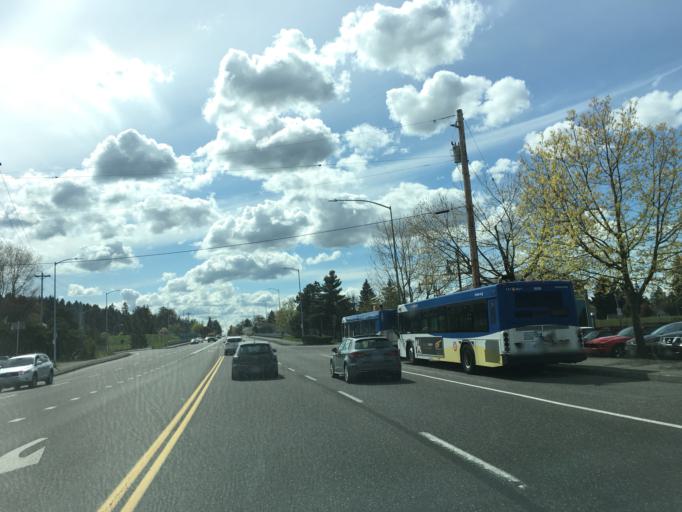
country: US
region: Oregon
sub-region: Multnomah County
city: Lents
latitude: 45.5582
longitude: -122.5644
